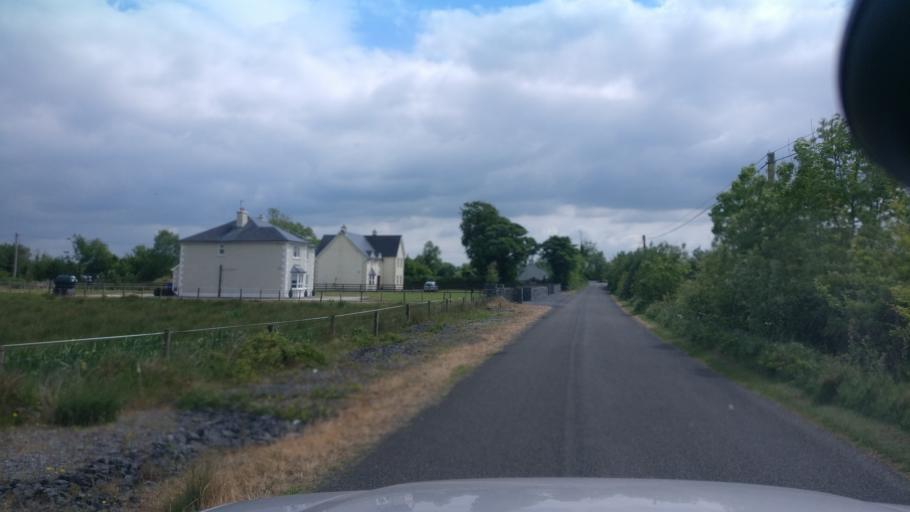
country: IE
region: Connaught
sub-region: County Galway
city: Ballinasloe
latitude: 53.2802
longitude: -8.3391
